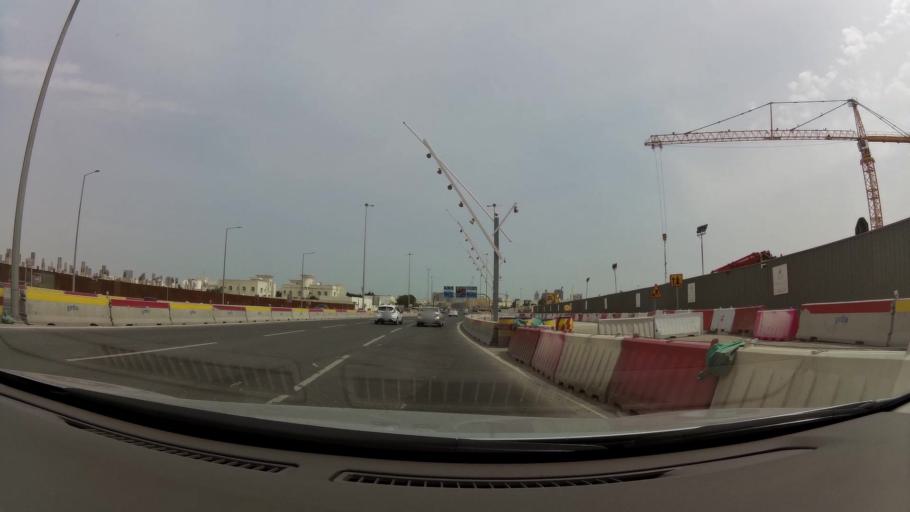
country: QA
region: Baladiyat ad Dawhah
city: Doha
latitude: 25.2734
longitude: 51.4858
